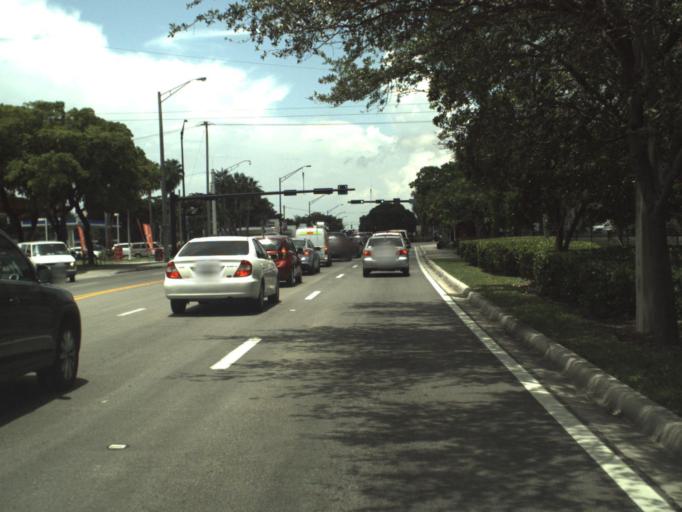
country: US
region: Florida
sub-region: Broward County
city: Oakland Park
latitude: 26.1657
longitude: -80.1315
